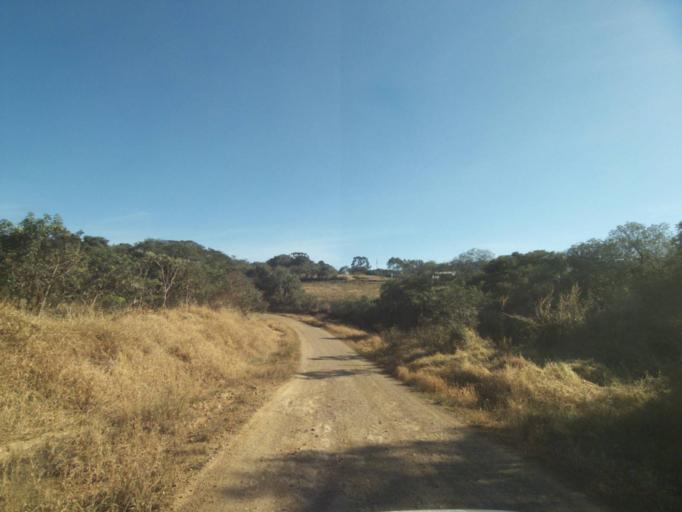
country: BR
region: Parana
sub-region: Tibagi
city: Tibagi
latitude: -24.5462
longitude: -50.5110
